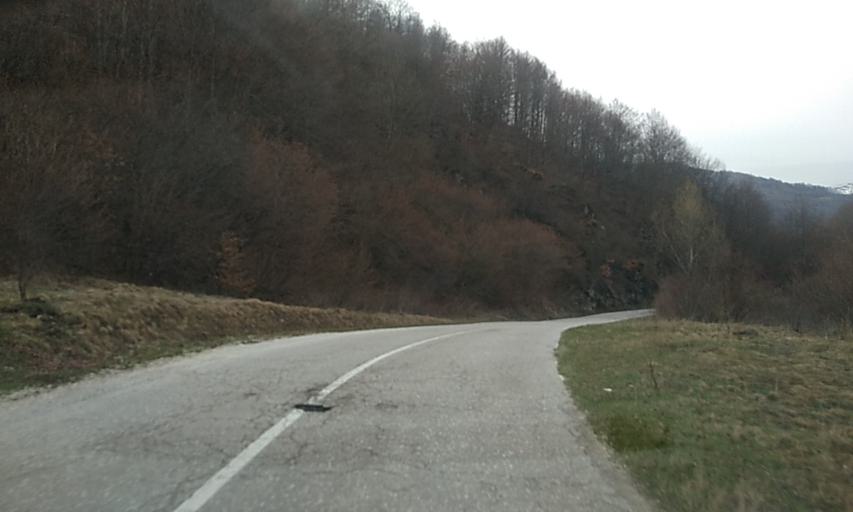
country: RS
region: Central Serbia
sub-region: Pcinjski Okrug
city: Bosilegrad
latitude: 42.5873
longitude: 22.4124
